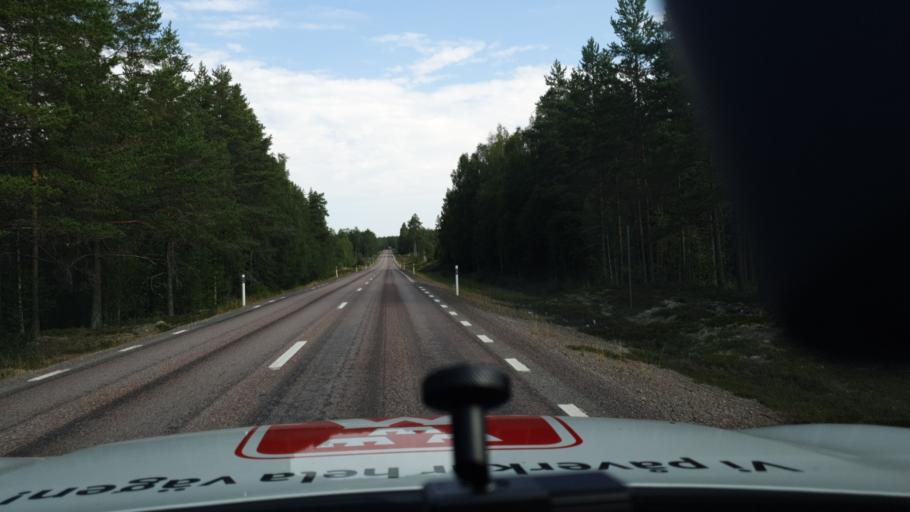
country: SE
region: Vaermland
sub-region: Hagfors Kommun
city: Ekshaerad
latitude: 60.4685
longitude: 13.3018
